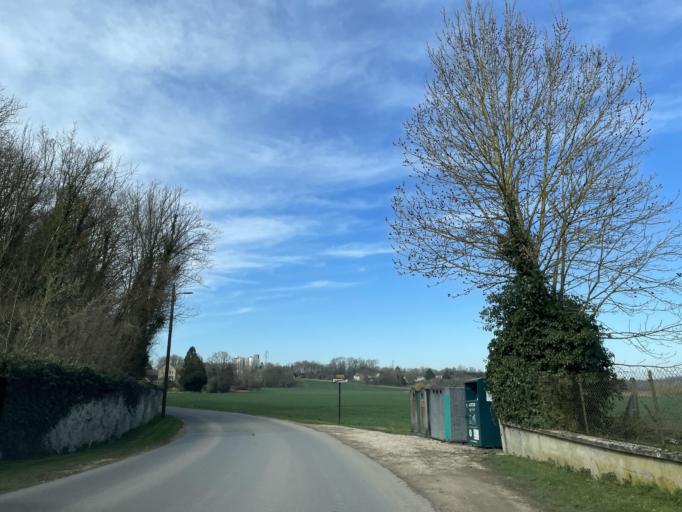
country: FR
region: Ile-de-France
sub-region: Departement de Seine-et-Marne
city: Chailly-en-Brie
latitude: 48.7410
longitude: 3.1252
